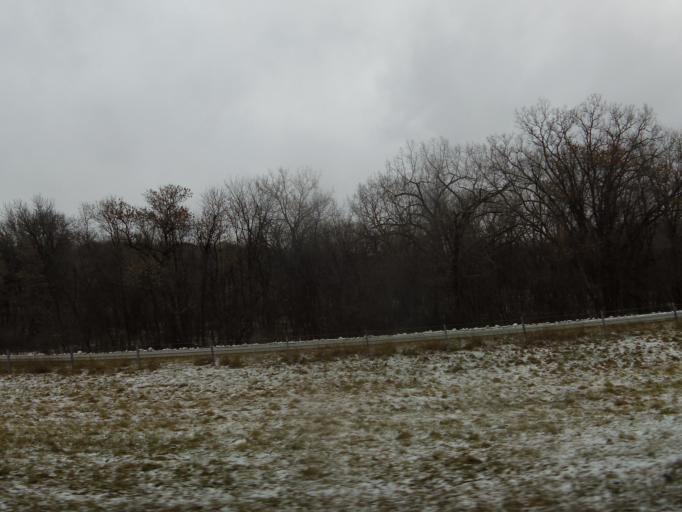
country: US
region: Minnesota
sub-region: Ramsey County
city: Maplewood
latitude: 44.9410
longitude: -93.0337
